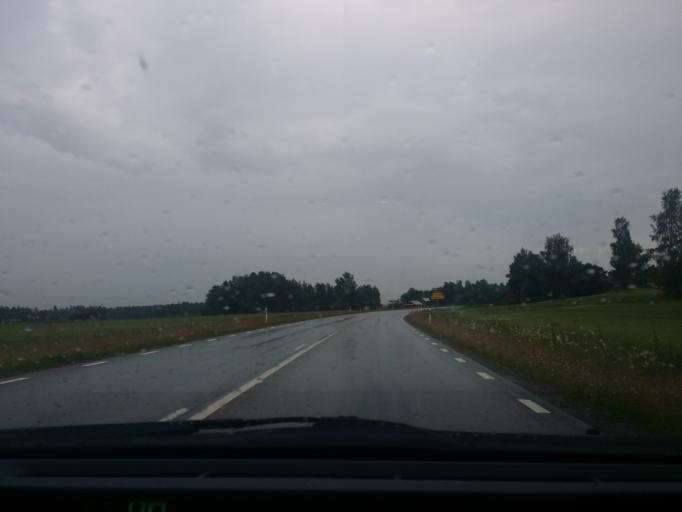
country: SE
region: OErebro
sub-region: Lindesbergs Kommun
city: Fellingsbro
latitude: 59.4501
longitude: 15.5893
